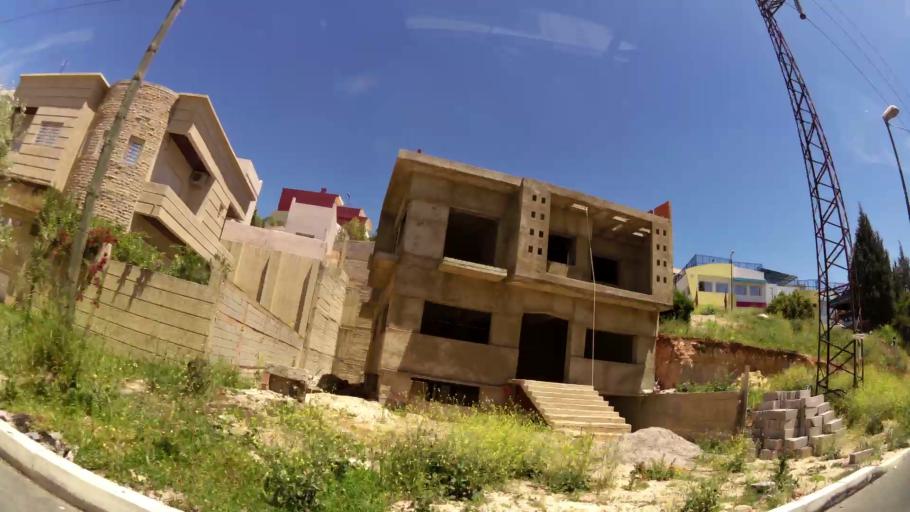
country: MA
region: Meknes-Tafilalet
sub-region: Meknes
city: Meknes
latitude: 33.9078
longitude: -5.5508
